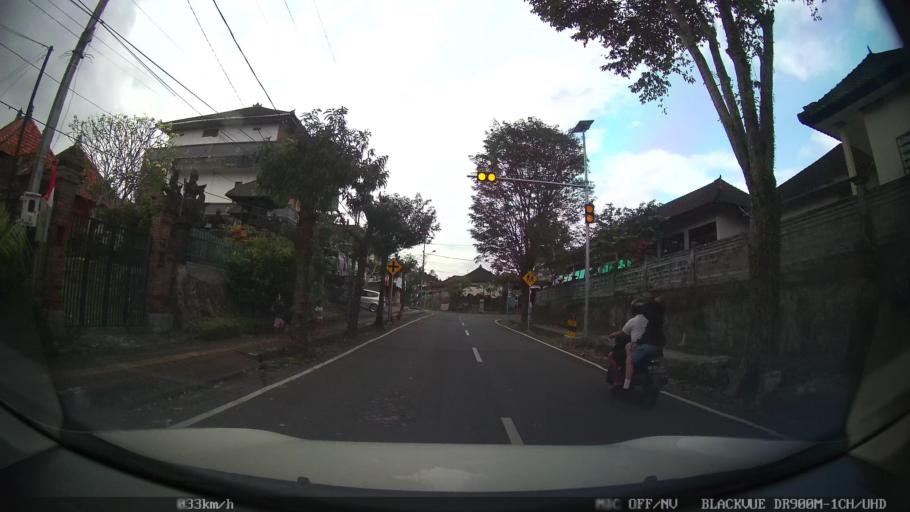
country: ID
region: Bali
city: Banjar Jambe Baleran
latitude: -8.5346
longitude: 115.1236
